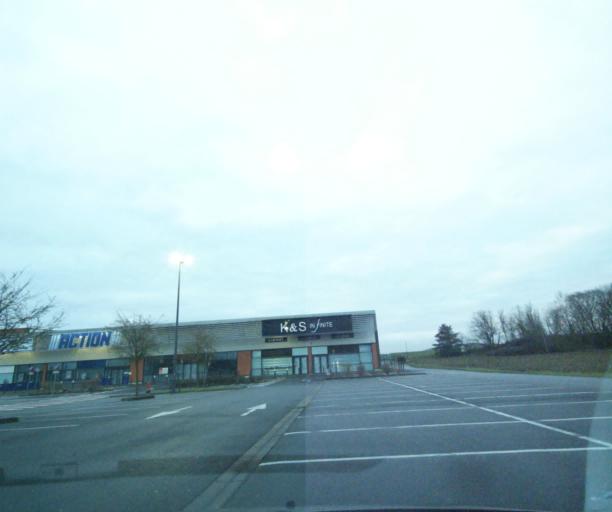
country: FR
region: Picardie
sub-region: Departement de l'Oise
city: Noyon
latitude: 49.5709
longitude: 2.9748
